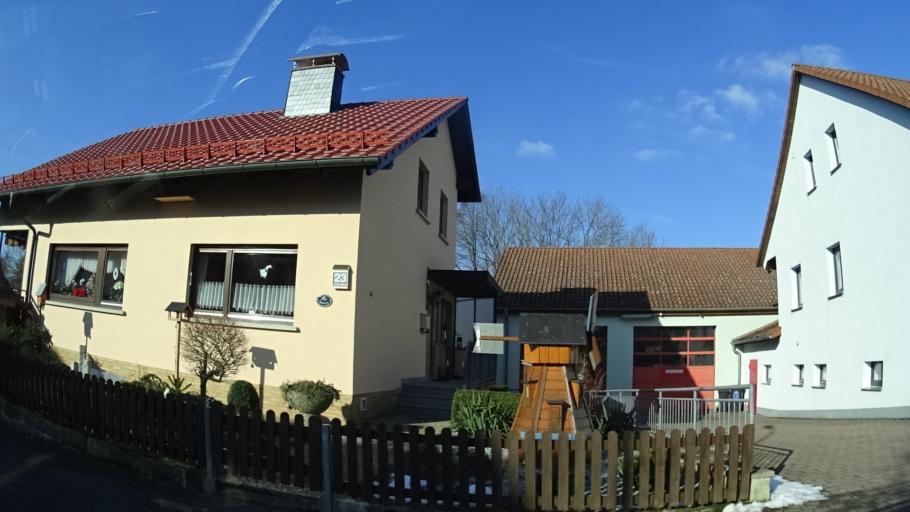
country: DE
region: Hesse
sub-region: Regierungsbezirk Kassel
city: Kalbach
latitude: 50.4046
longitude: 9.6784
